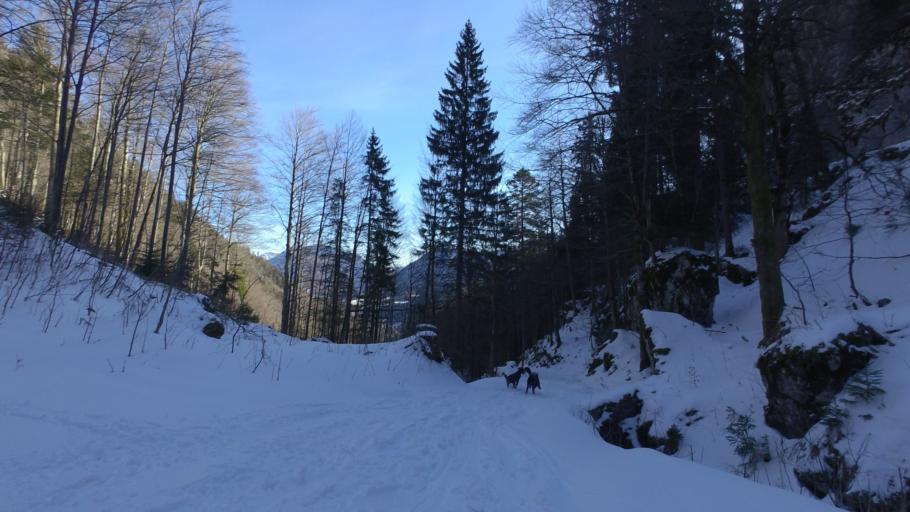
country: DE
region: Bavaria
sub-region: Upper Bavaria
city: Bergen
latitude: 47.7549
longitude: 12.5897
